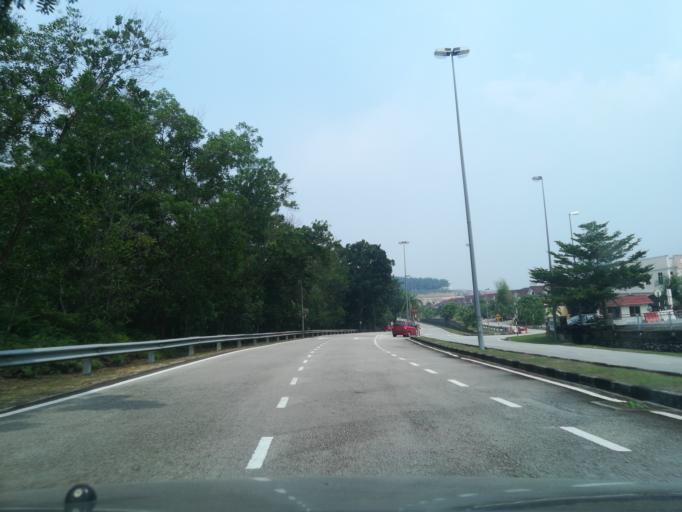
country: MY
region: Kedah
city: Kulim
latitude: 5.3965
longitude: 100.5805
